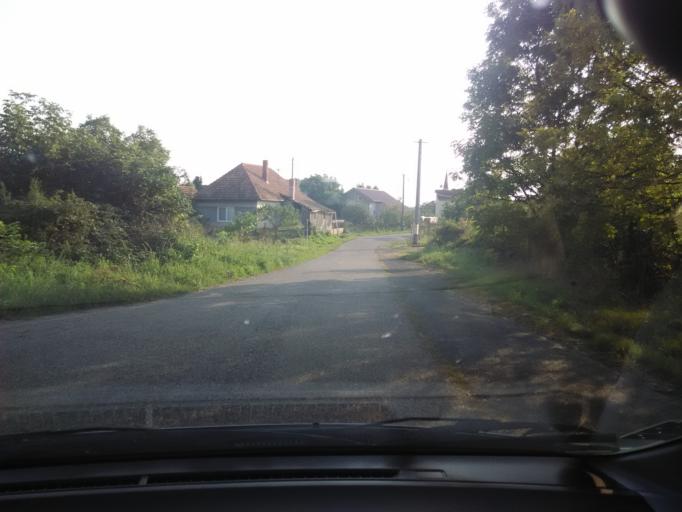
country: SK
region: Nitriansky
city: Levice
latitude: 48.2887
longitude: 18.6995
